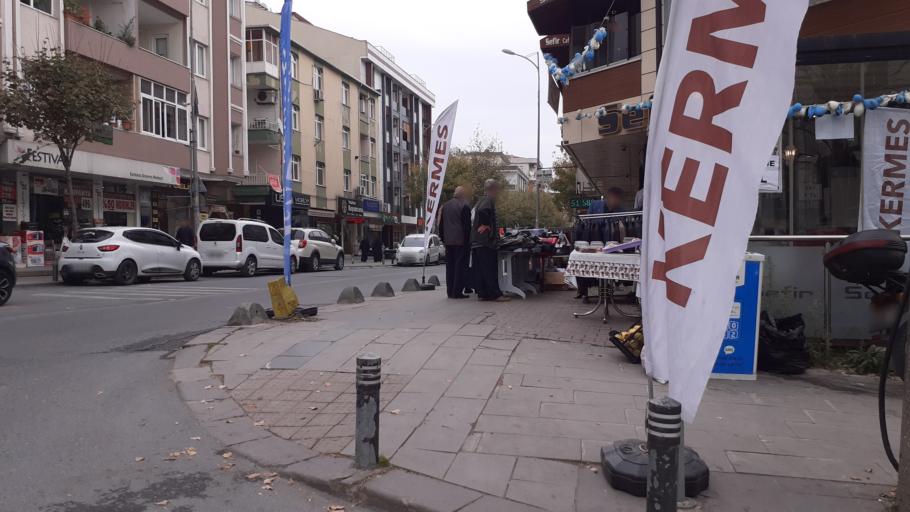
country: TR
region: Istanbul
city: Mahmutbey
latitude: 40.9924
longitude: 28.7838
